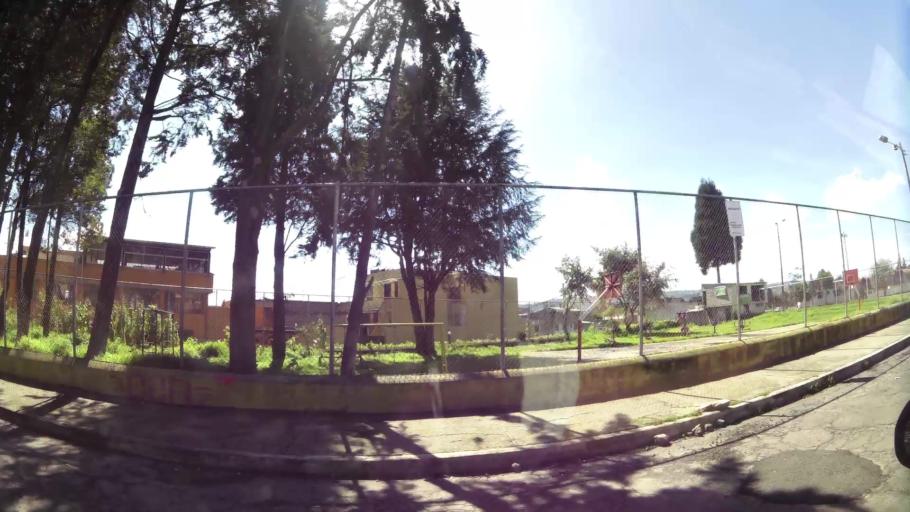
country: EC
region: Pichincha
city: Quito
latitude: -0.2867
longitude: -78.5597
